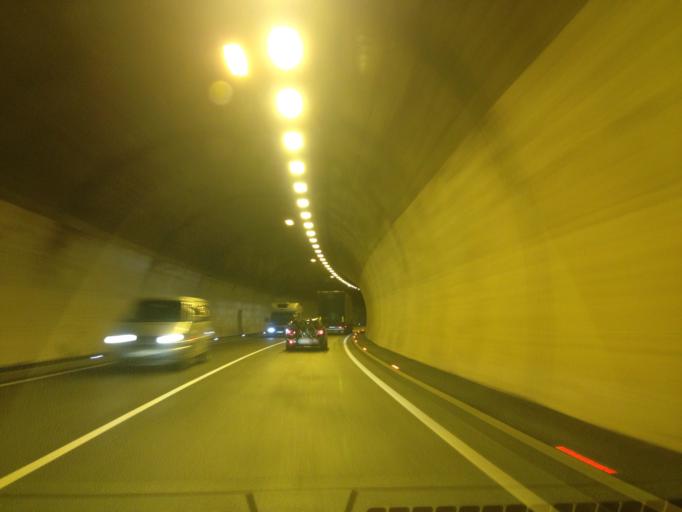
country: AT
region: Tyrol
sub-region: Politischer Bezirk Imst
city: Nassereith
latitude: 47.3068
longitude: 10.8375
